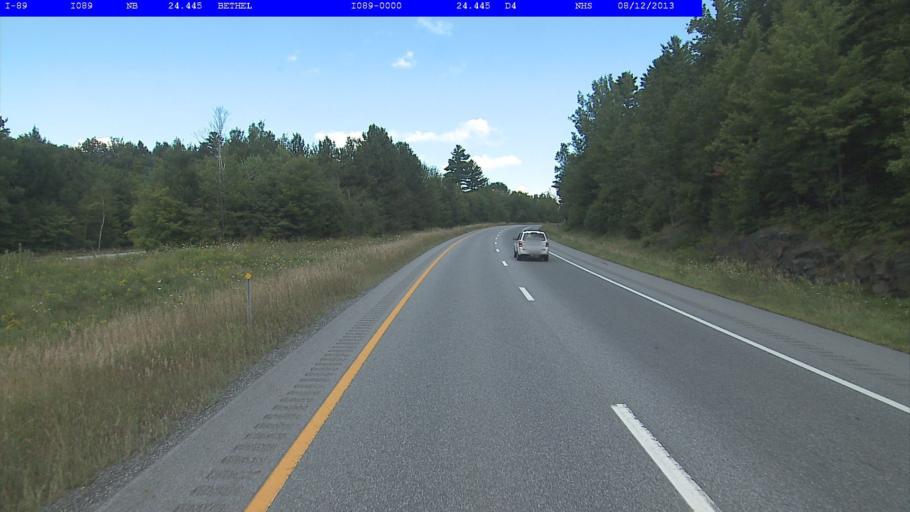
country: US
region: Vermont
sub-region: Orange County
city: Randolph
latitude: 43.8535
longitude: -72.6057
